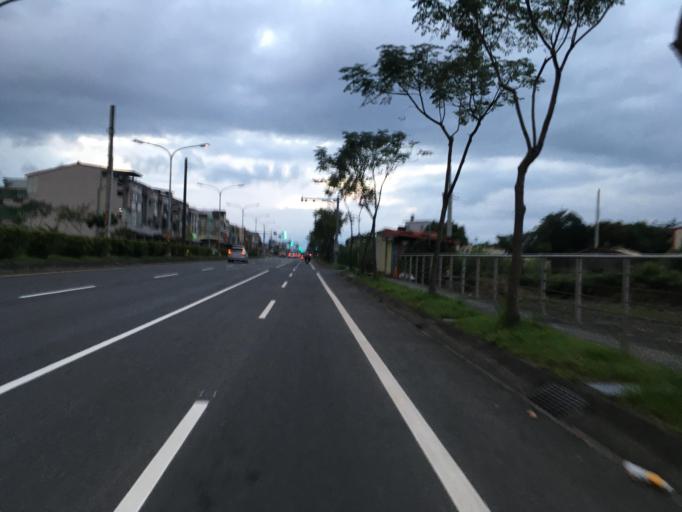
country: TW
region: Taiwan
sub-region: Yilan
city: Yilan
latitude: 24.6206
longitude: 121.8420
